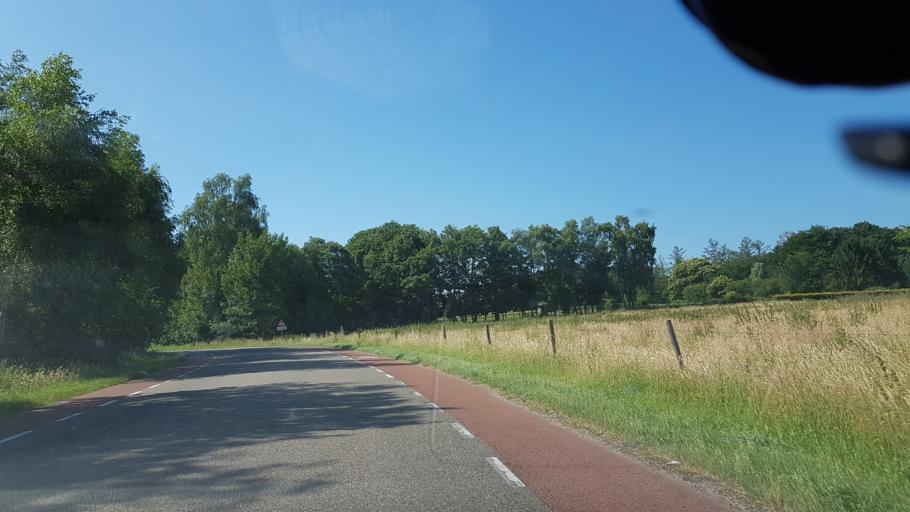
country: NL
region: Gelderland
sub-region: Gemeente Groesbeek
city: Bredeweg
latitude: 51.7428
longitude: 5.9523
